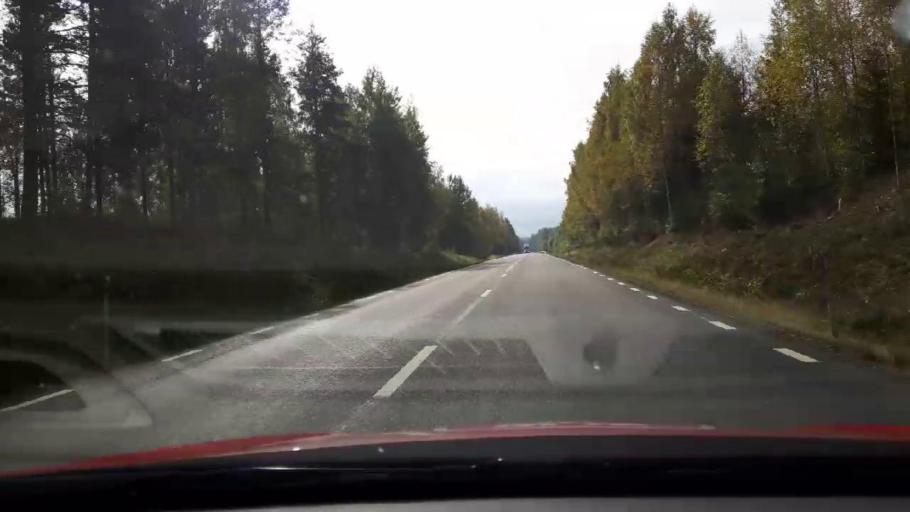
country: SE
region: Gaevleborg
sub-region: Bollnas Kommun
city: Arbra
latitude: 61.4809
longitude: 16.3655
